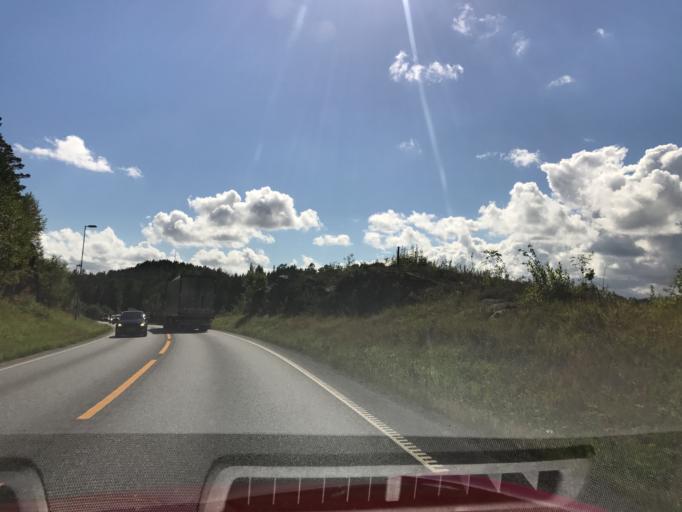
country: NO
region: Telemark
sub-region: Kragero
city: Kragero
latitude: 58.9693
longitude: 9.4926
